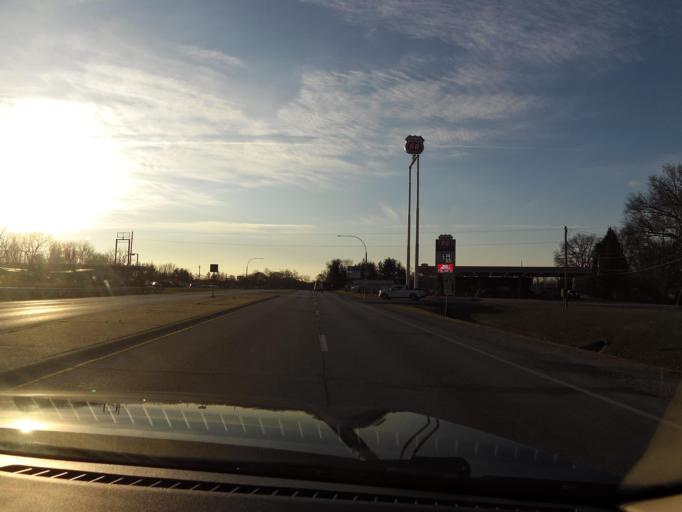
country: US
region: Illinois
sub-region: Fayette County
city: Vandalia
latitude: 38.9755
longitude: -89.0950
